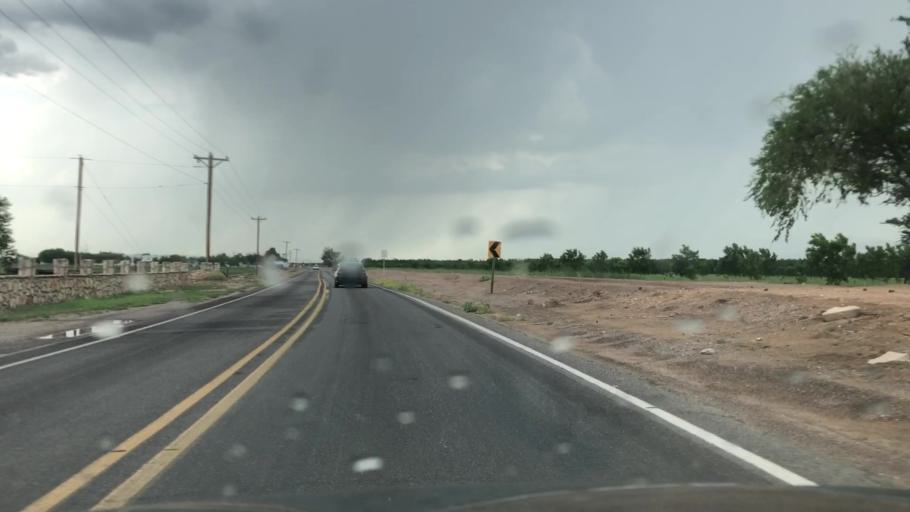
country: US
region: New Mexico
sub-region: Dona Ana County
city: Berino
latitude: 32.0545
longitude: -106.6753
